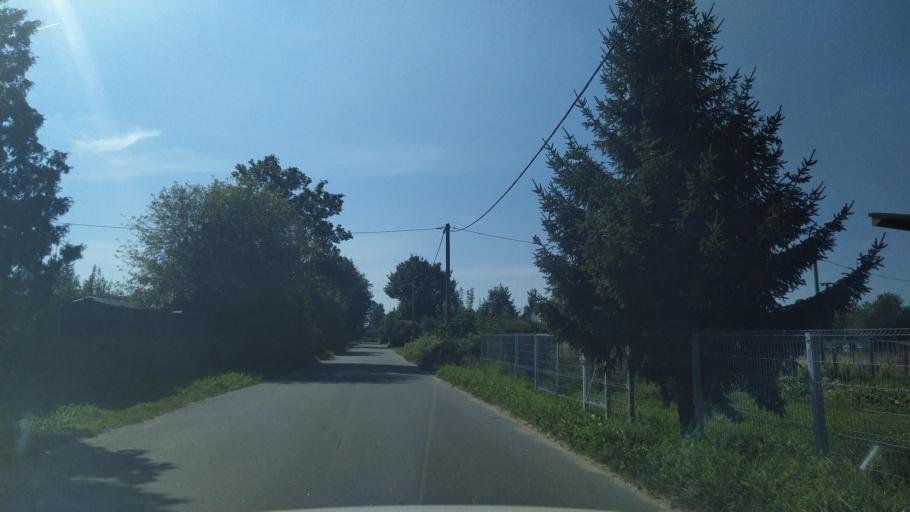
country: RU
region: Leningrad
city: Siverskiy
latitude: 59.2682
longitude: 30.0431
